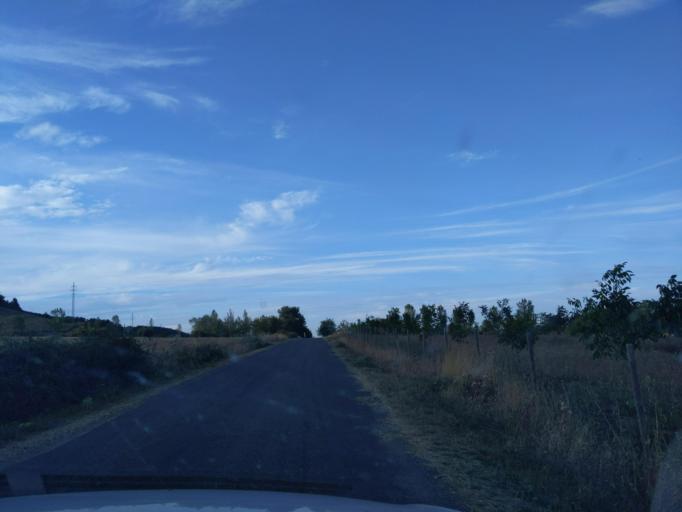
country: ES
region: La Rioja
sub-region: Provincia de La Rioja
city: Santurdejo
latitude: 42.3803
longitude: -2.9844
